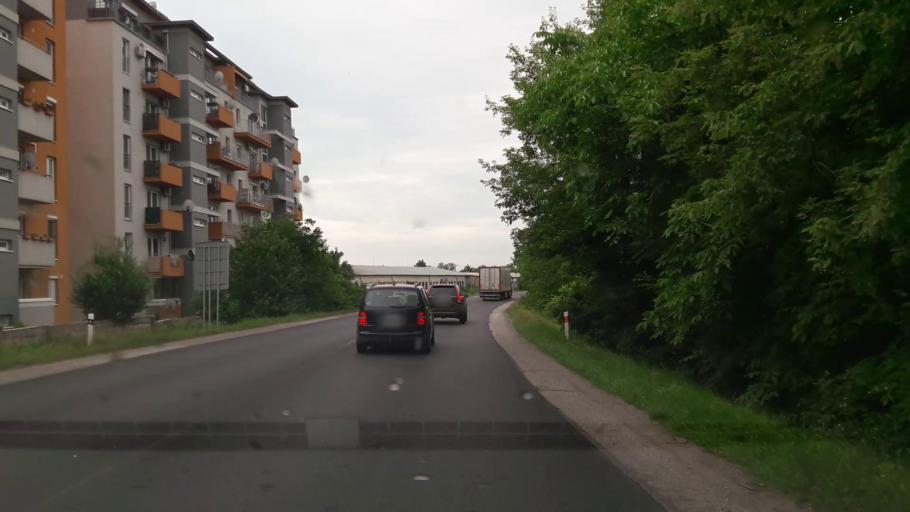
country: SK
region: Bratislavsky
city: Senec
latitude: 48.2218
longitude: 17.3856
